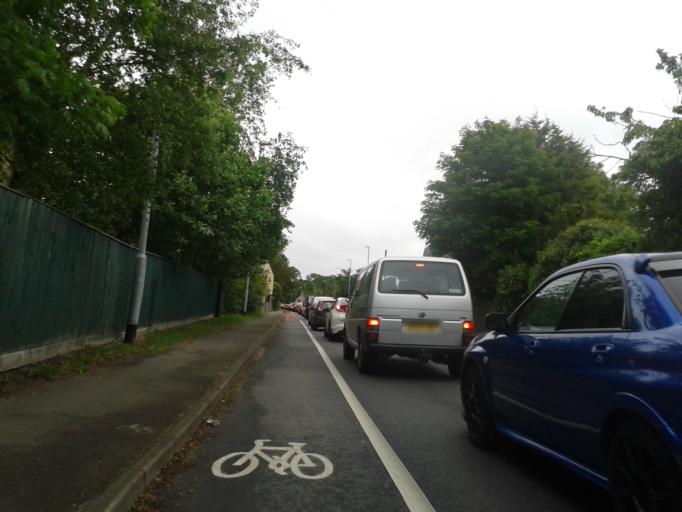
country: GB
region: England
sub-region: Cambridgeshire
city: Histon
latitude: 52.2471
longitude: 0.1098
